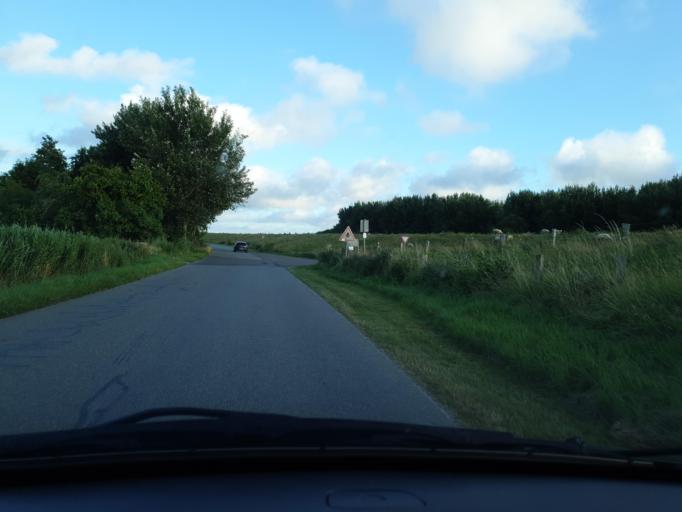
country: DE
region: Schleswig-Holstein
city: Elpersbuttel
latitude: 54.0691
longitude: 9.0141
